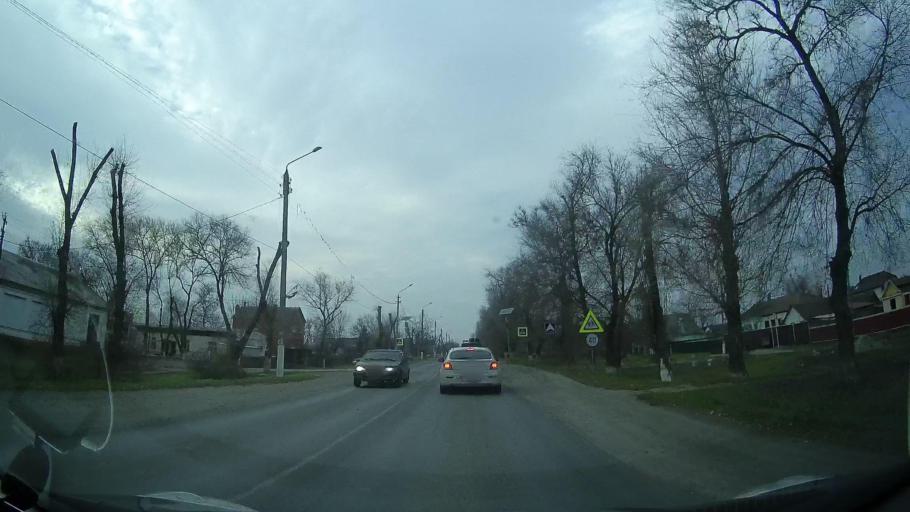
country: RU
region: Rostov
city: Ol'ginskaya
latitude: 47.1873
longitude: 39.9521
